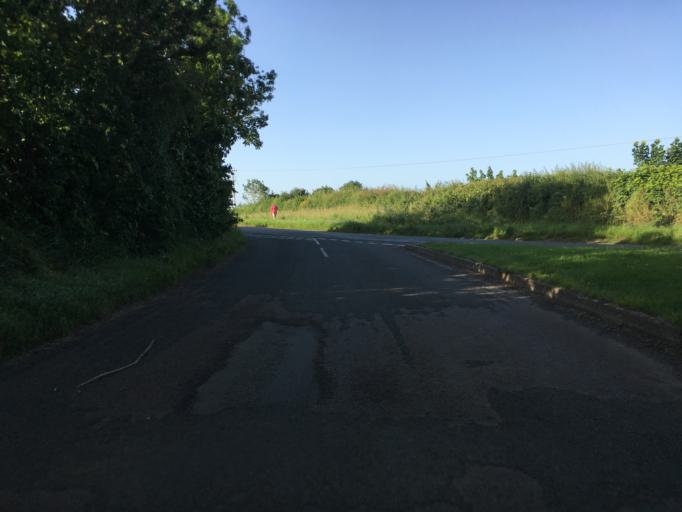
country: GB
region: England
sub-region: Gloucestershire
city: Fairford
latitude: 51.7125
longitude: -1.7682
